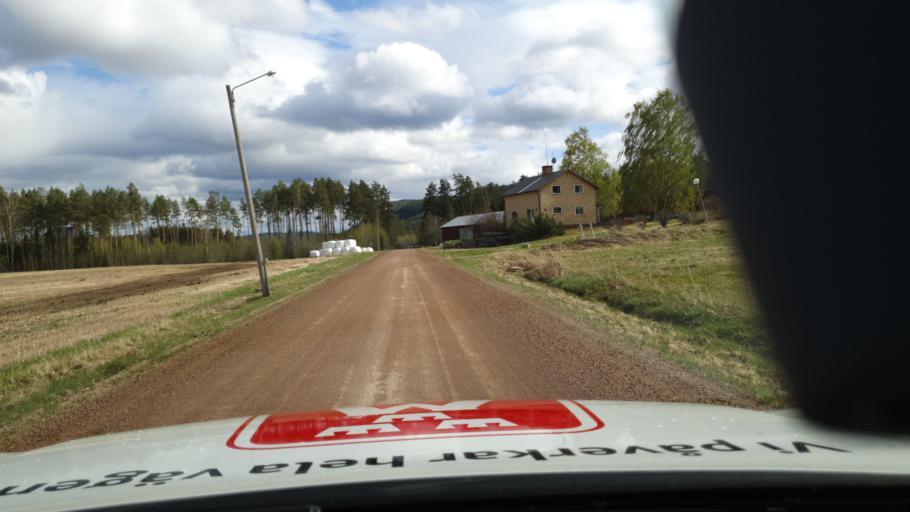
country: SE
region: Jaemtland
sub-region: Ragunda Kommun
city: Hammarstrand
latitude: 63.0902
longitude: 16.3320
